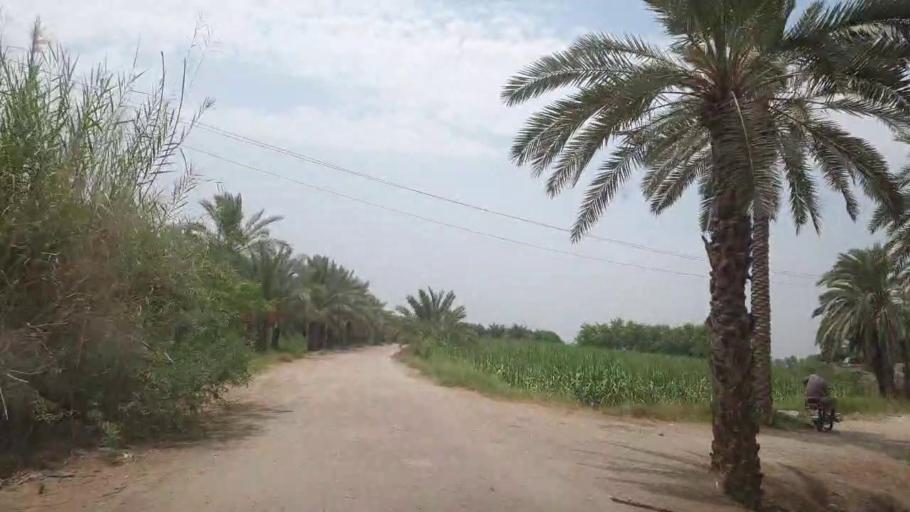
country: PK
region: Sindh
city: Kot Diji
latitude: 27.4413
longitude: 68.6824
